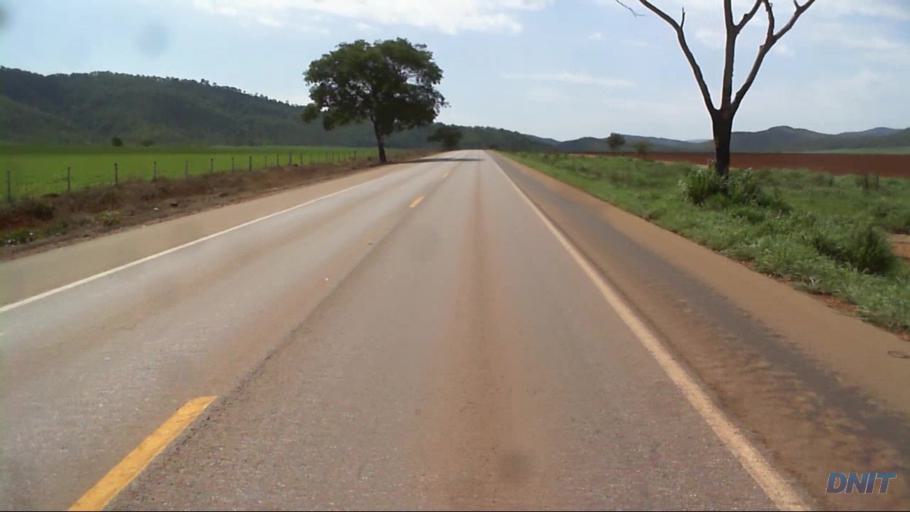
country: BR
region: Goias
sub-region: Barro Alto
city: Barro Alto
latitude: -15.1112
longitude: -48.8429
